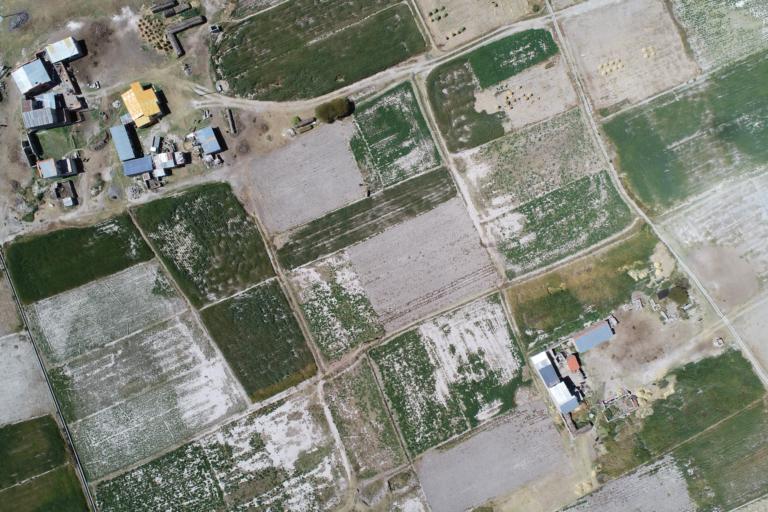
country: BO
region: La Paz
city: Achacachi
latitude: -16.0147
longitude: -68.7204
